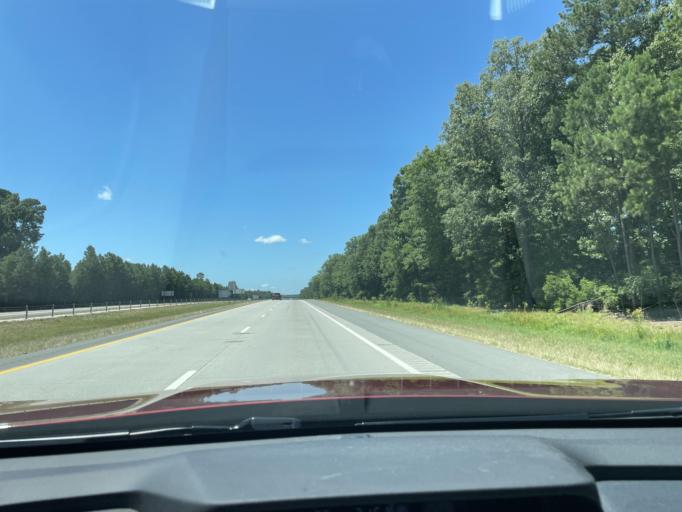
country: US
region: Arkansas
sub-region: Jefferson County
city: Pine Bluff
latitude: 34.1911
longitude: -91.9795
